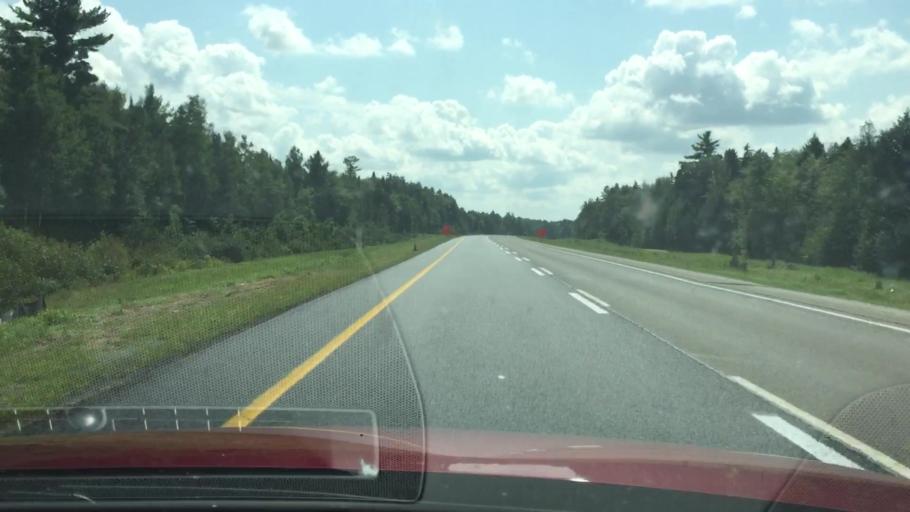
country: US
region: Maine
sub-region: Penobscot County
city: Medway
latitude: 45.6939
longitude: -68.4877
